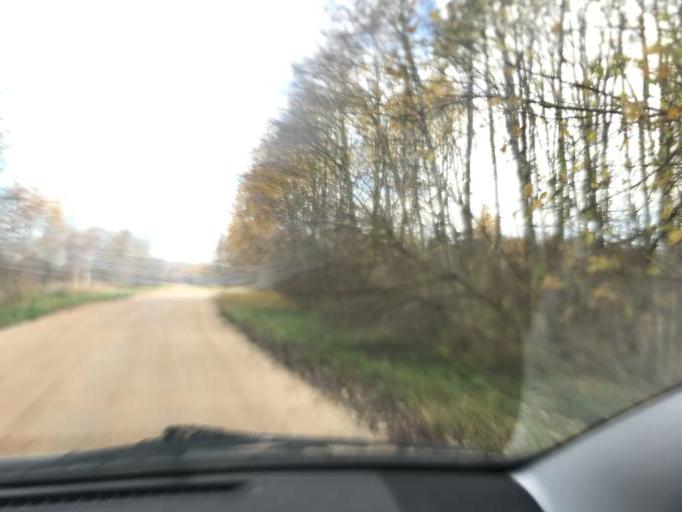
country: BY
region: Vitebsk
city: Haradok
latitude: 55.4535
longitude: 30.0386
